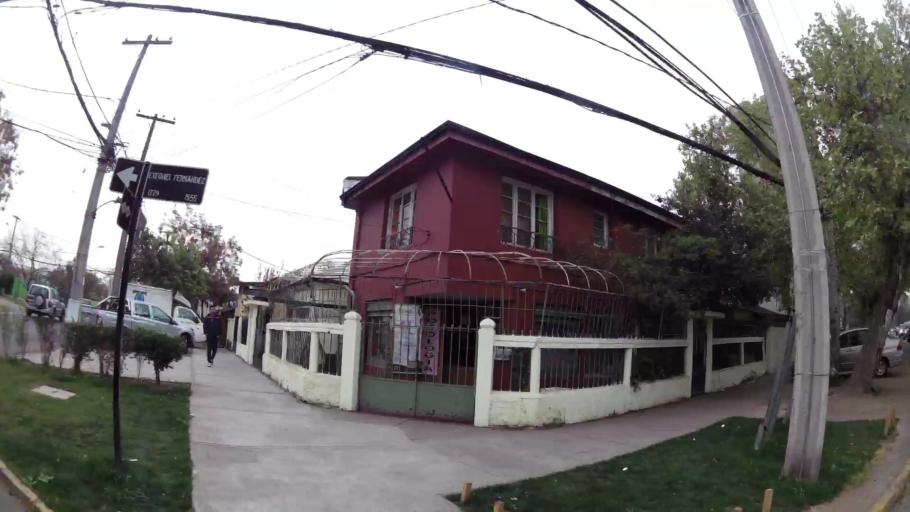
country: CL
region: Santiago Metropolitan
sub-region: Provincia de Santiago
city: Villa Presidente Frei, Nunoa, Santiago, Chile
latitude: -33.4709
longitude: -70.6007
